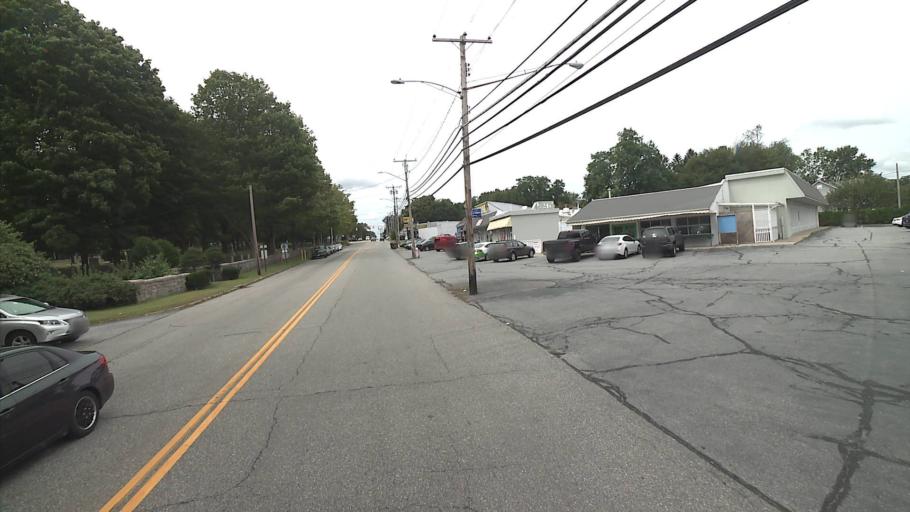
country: US
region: Connecticut
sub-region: New London County
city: Central Waterford
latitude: 41.3668
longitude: -72.1237
